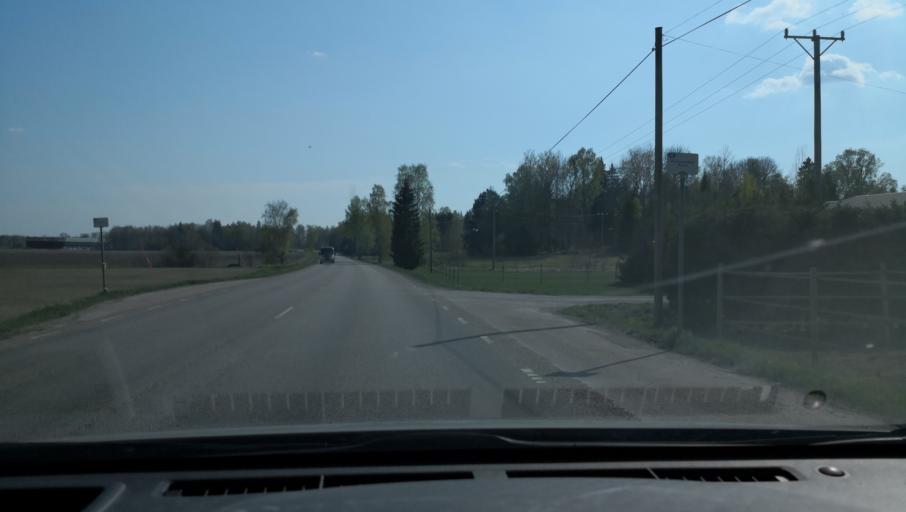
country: SE
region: Vaestmanland
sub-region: Sala Kommun
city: Sala
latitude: 59.9509
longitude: 16.6165
